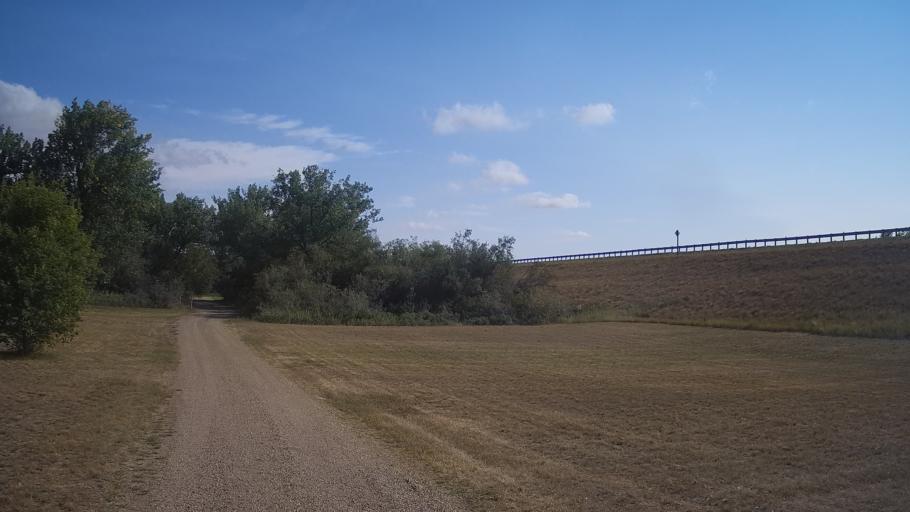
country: CA
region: Alberta
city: Brooks
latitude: 50.9156
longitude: -111.9005
